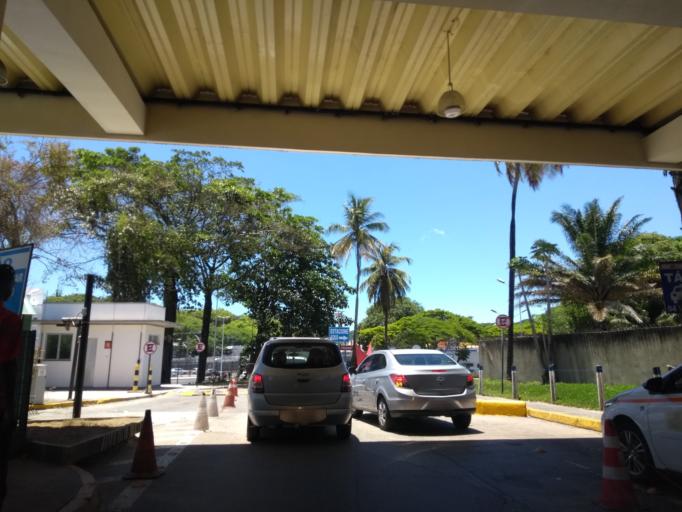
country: BR
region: Bahia
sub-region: Salvador
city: Salvador
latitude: -12.9785
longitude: -38.4661
